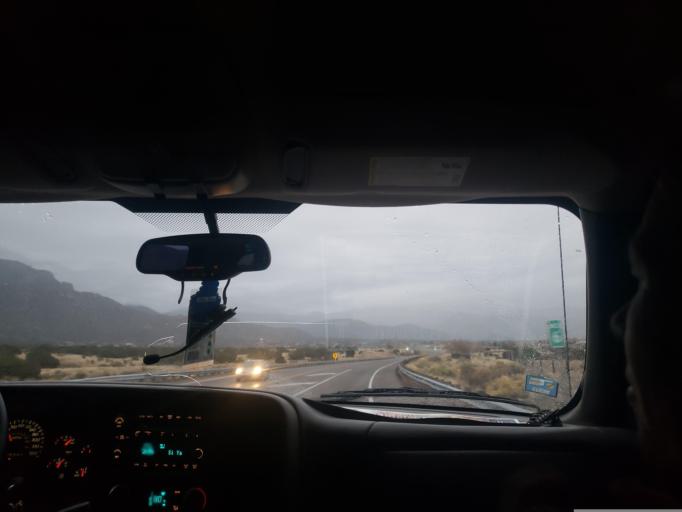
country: US
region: New Mexico
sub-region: Bernalillo County
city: Sandia Heights
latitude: 35.2001
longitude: -106.5063
